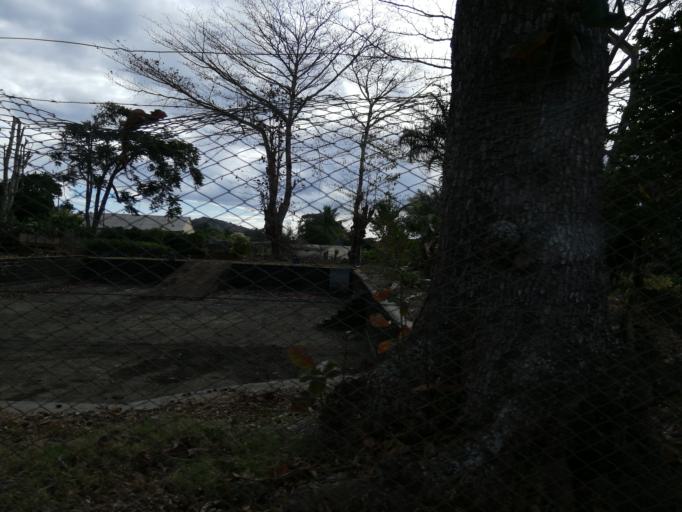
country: MU
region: Black River
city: Petite Riviere
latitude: -20.2260
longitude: 57.4618
